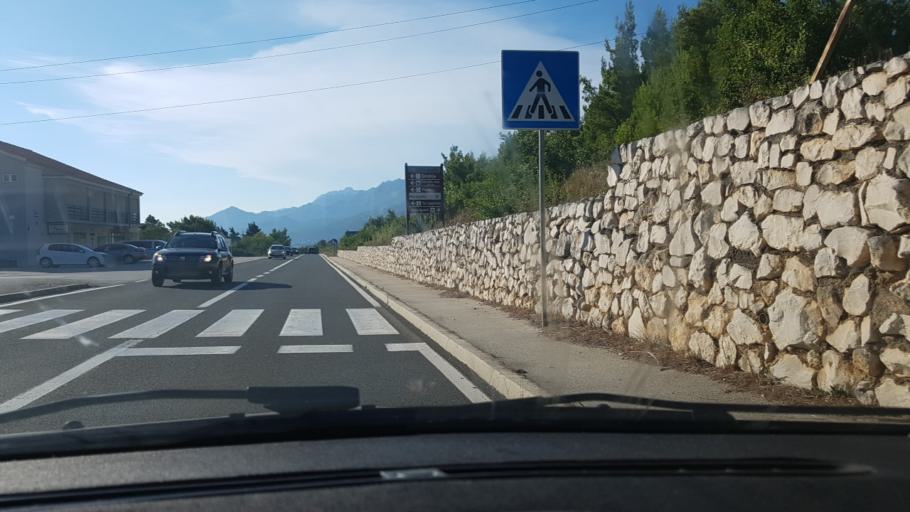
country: HR
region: Zadarska
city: Posedarje
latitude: 44.2530
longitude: 15.5394
